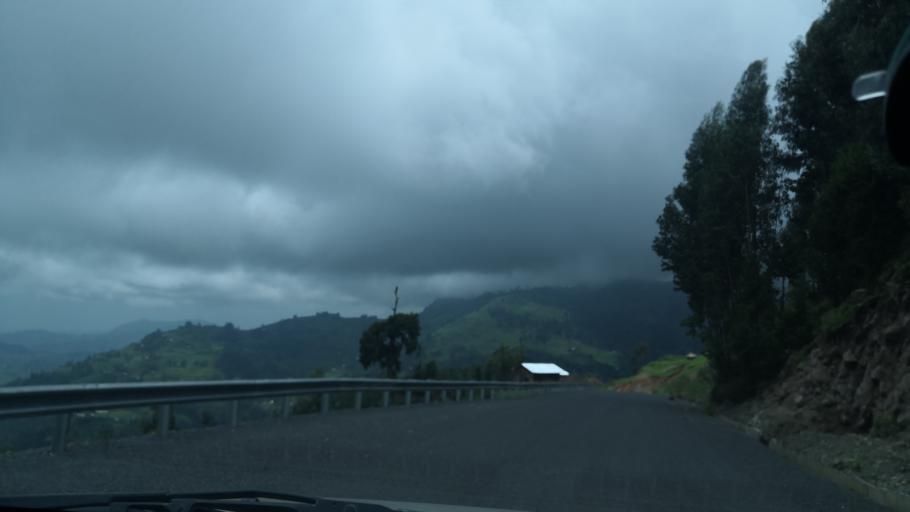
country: ET
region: Amhara
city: Abomsa
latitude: 10.3317
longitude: 39.8407
